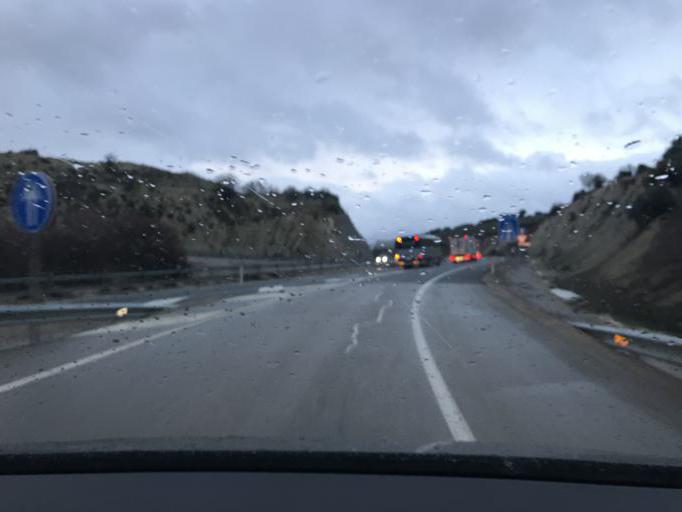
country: ES
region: Andalusia
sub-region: Provincia de Granada
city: Campotejar
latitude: 37.4691
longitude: -3.5709
